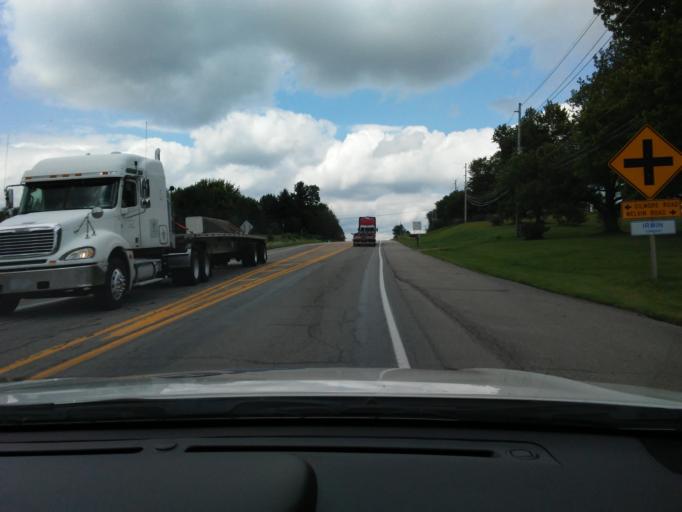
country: US
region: Pennsylvania
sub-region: Mercer County
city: Grove City
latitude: 41.2092
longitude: -79.9740
